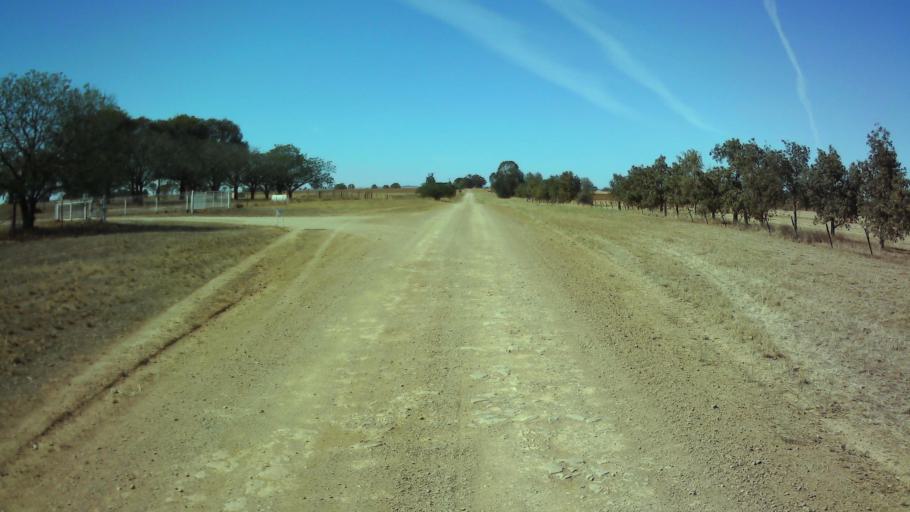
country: AU
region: New South Wales
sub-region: Weddin
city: Grenfell
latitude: -34.0553
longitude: 148.1719
